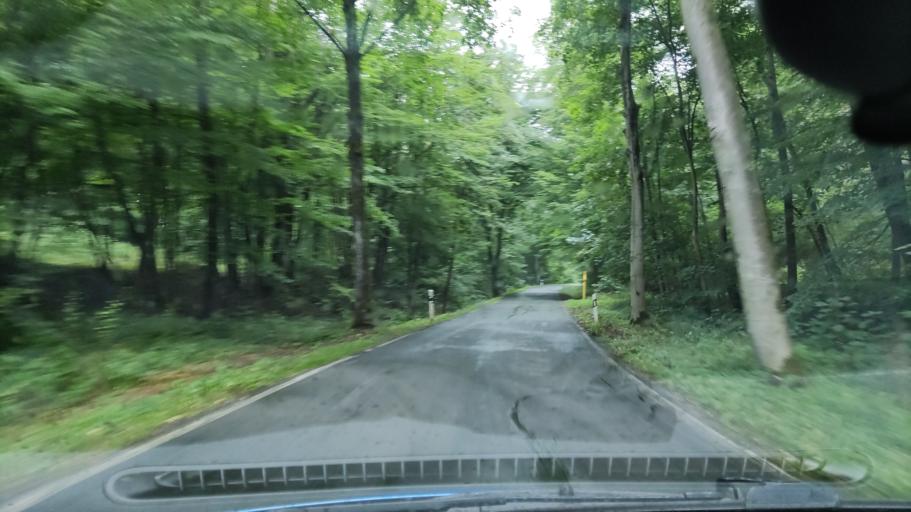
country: DE
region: Lower Saxony
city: Coppengrave
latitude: 51.9629
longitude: 9.7653
